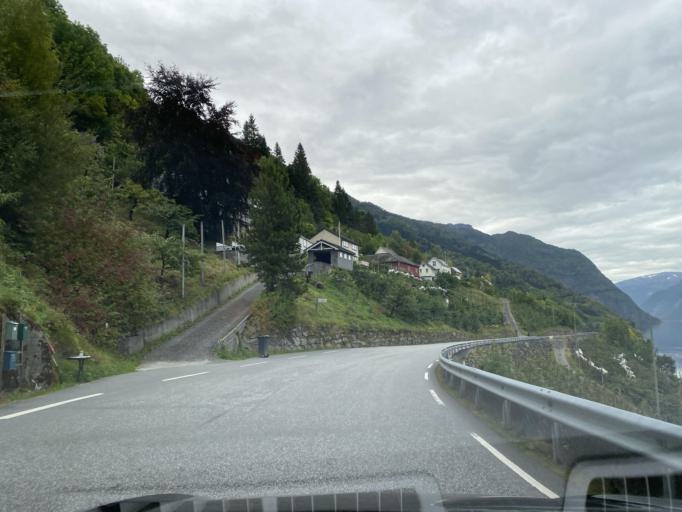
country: NO
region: Hordaland
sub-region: Odda
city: Odda
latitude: 60.2136
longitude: 6.6032
